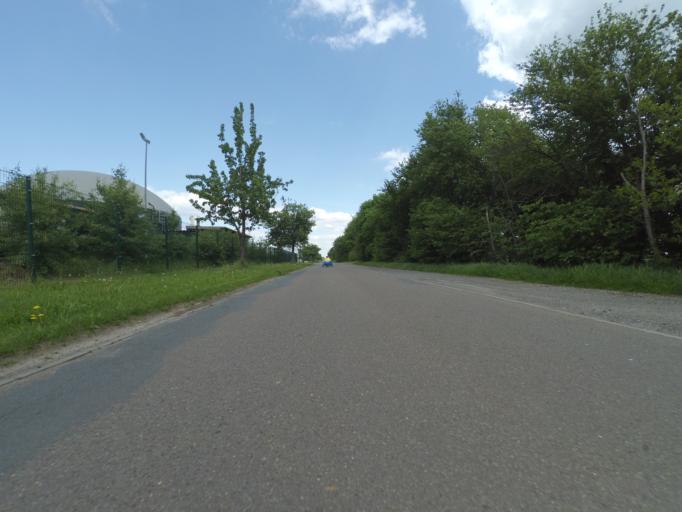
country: DE
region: Lower Saxony
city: Muden
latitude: 52.5315
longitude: 10.3775
